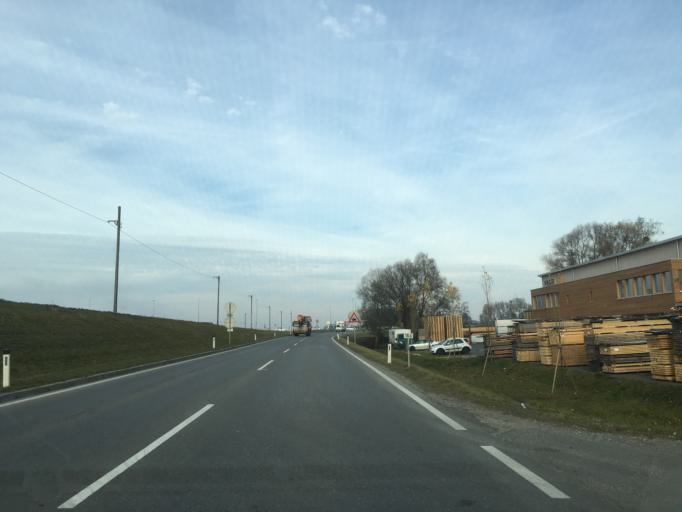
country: AT
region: Vorarlberg
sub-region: Politischer Bezirk Bregenz
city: Fussach
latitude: 47.4759
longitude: 9.6713
